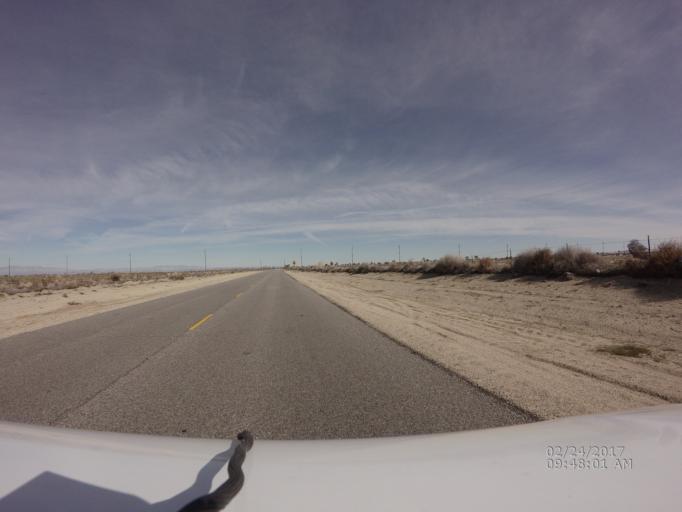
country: US
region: California
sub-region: Los Angeles County
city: Littlerock
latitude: 34.6288
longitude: -118.0053
